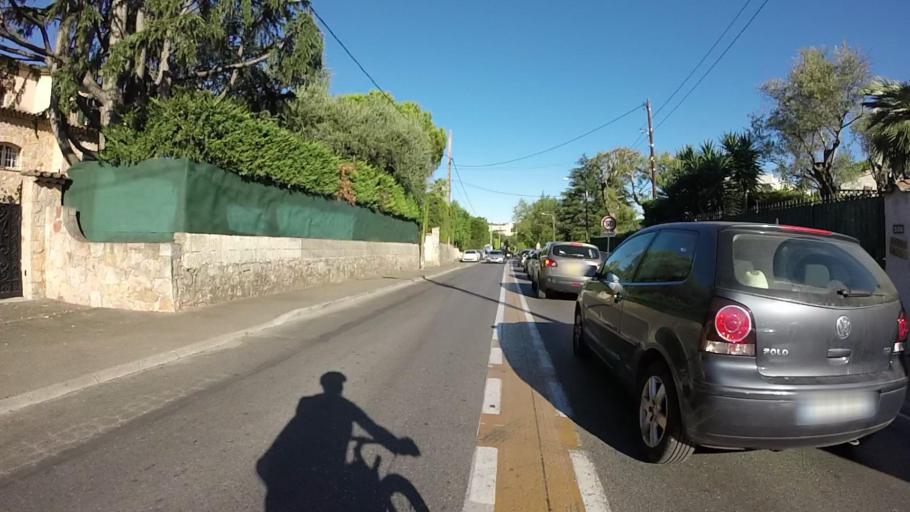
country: FR
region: Provence-Alpes-Cote d'Azur
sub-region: Departement des Alpes-Maritimes
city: Antibes
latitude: 43.5839
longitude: 7.1059
